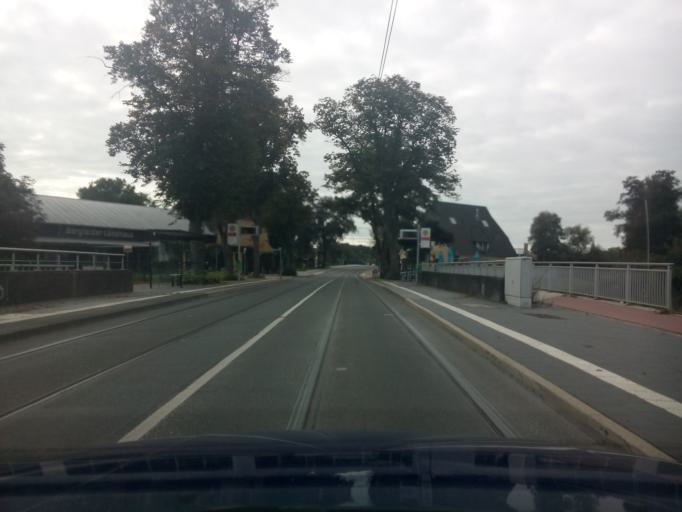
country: DE
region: Lower Saxony
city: Lilienthal
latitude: 53.1356
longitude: 8.8987
